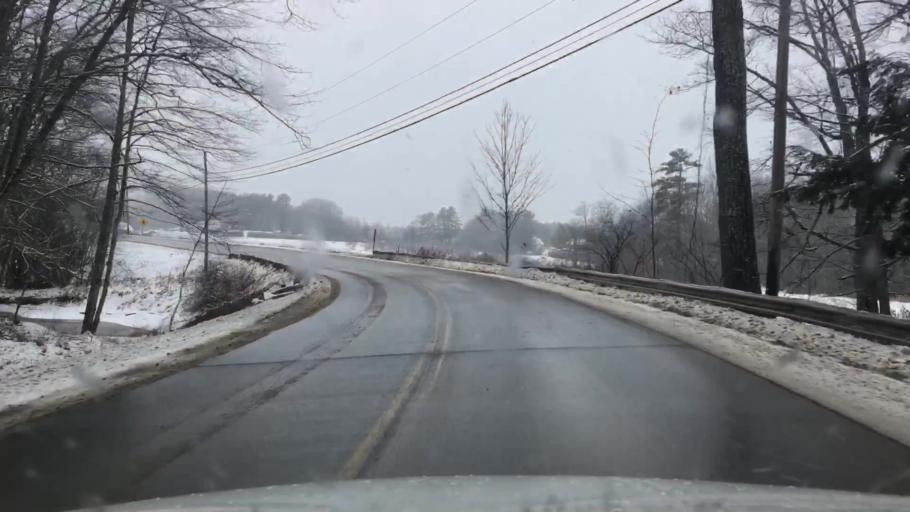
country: US
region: Maine
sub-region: Knox County
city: Warren
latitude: 44.1541
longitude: -69.2844
